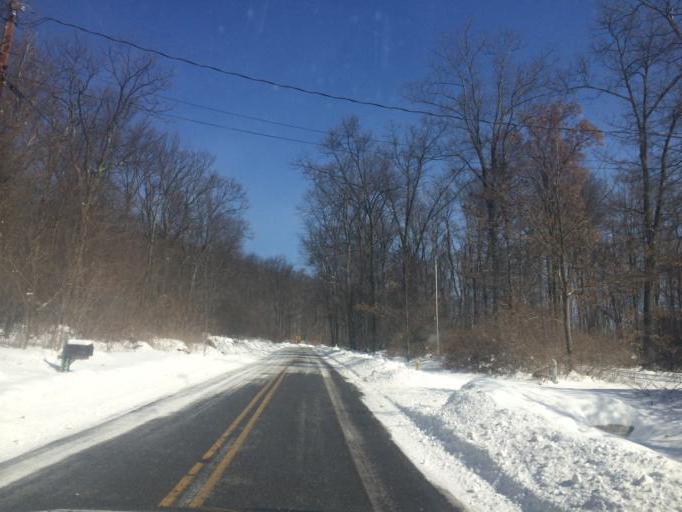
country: US
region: Pennsylvania
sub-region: Centre County
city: Stormstown
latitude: 40.8686
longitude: -78.0307
